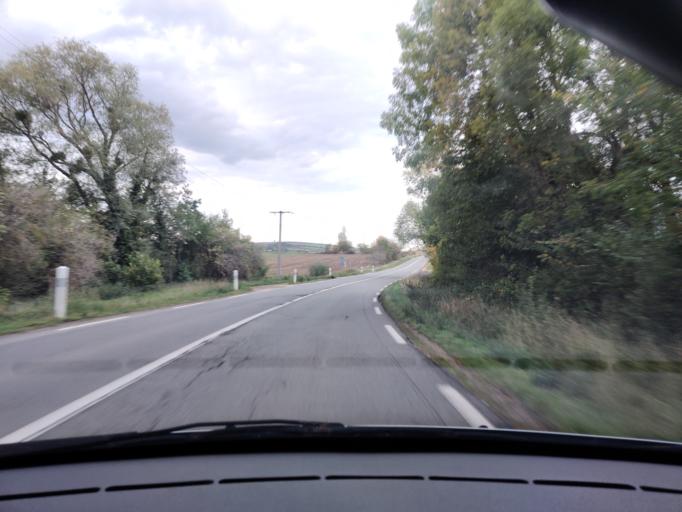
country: FR
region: Auvergne
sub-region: Departement du Puy-de-Dome
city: Saint-Bonnet-pres-Riom
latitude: 45.9494
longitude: 3.1076
